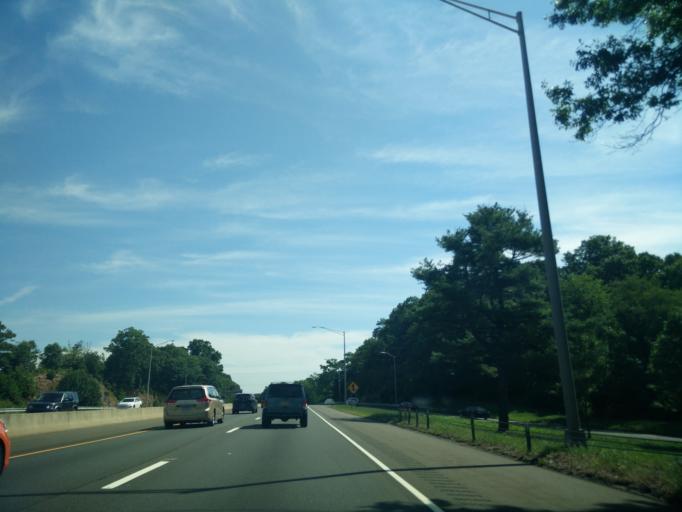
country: US
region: Connecticut
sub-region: New Haven County
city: Branford
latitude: 41.2882
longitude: -72.8195
